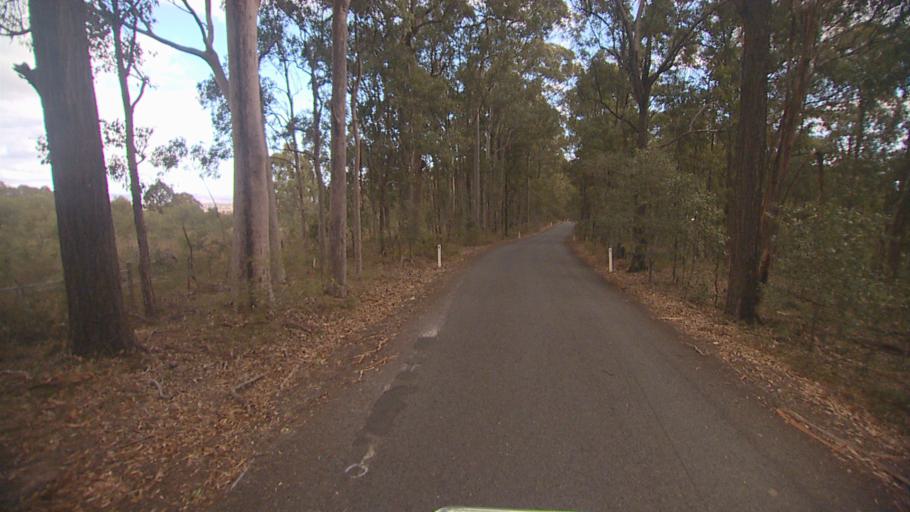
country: AU
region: Queensland
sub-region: Logan
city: Cedar Vale
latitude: -27.9007
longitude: 153.0353
